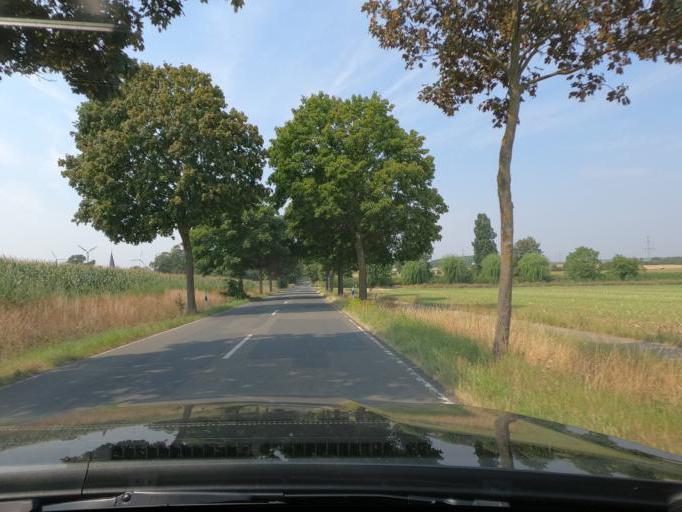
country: DE
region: Lower Saxony
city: Algermissen
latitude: 52.2718
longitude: 9.9315
